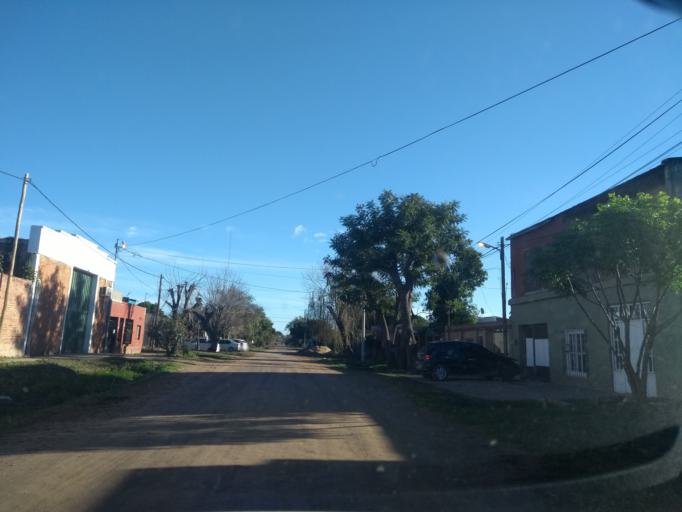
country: AR
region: Chaco
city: Barranqueras
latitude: -27.4759
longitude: -58.9301
